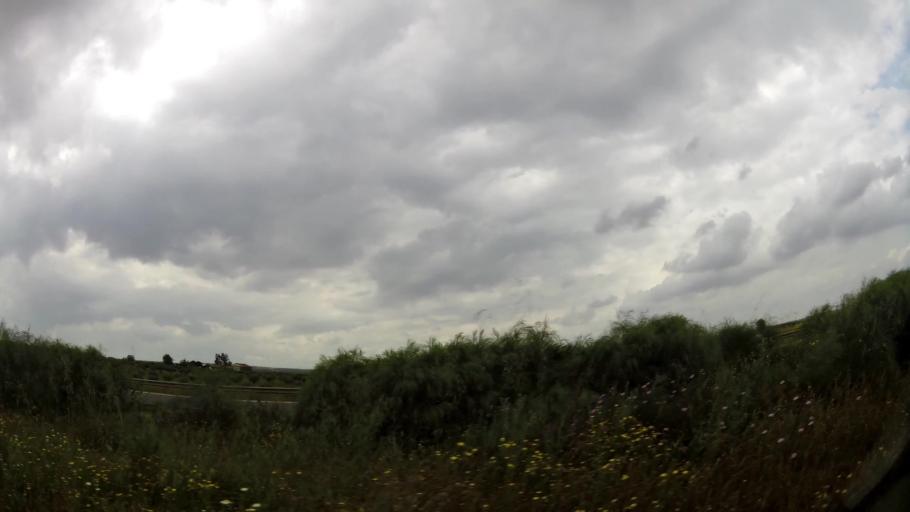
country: MA
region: Rabat-Sale-Zemmour-Zaer
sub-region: Khemisset
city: Tiflet
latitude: 33.8922
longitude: -6.3642
